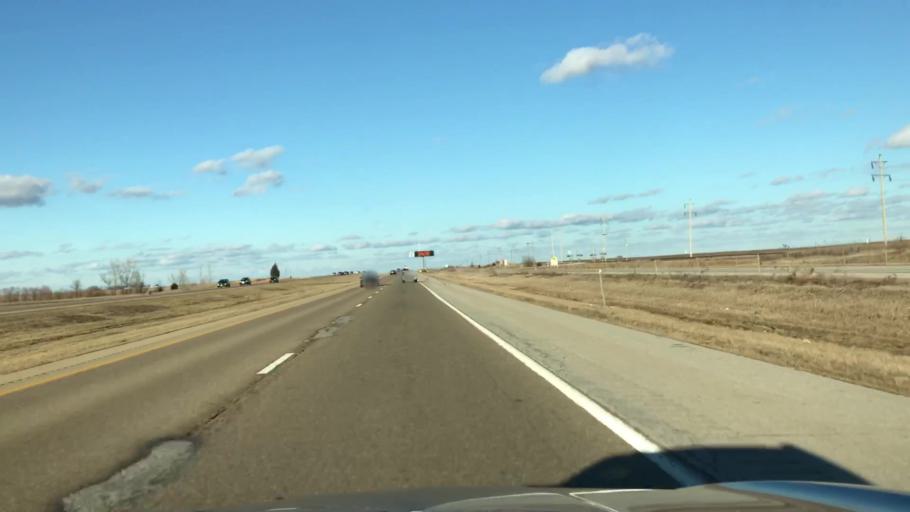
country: US
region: Illinois
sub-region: McLean County
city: Chenoa
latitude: 40.6953
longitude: -88.7523
